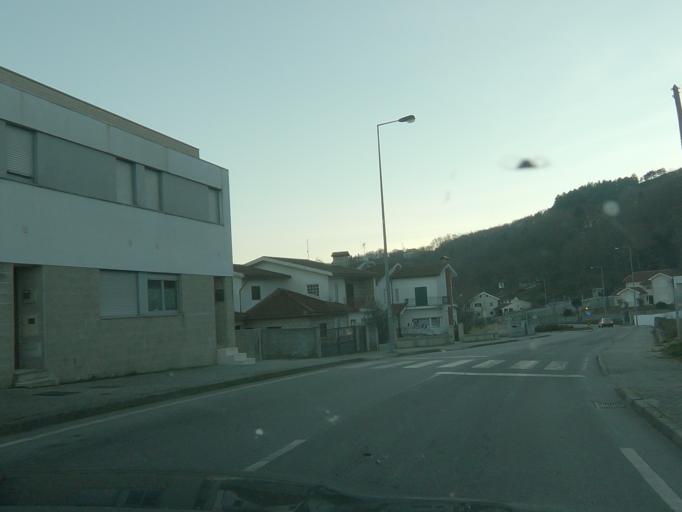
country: PT
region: Vila Real
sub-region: Vila Pouca de Aguiar
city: Vila Pouca de Aguiar
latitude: 41.4985
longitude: -7.6476
